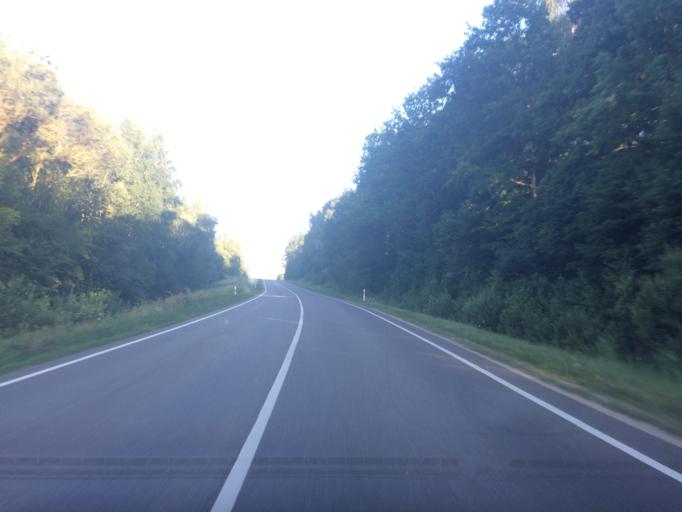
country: LT
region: Utenos apskritis
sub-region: Anyksciai
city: Anyksciai
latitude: 55.4041
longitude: 25.1313
